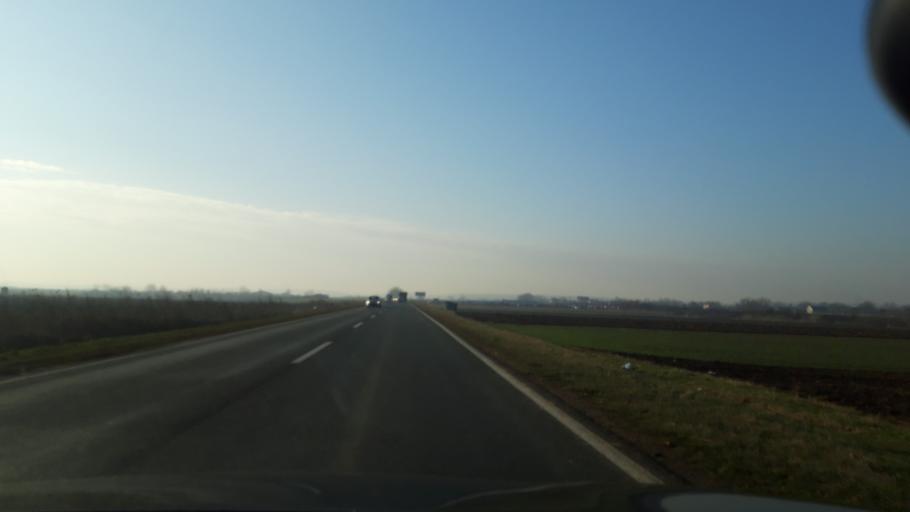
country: RS
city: Klenak
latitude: 44.7920
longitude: 19.7256
